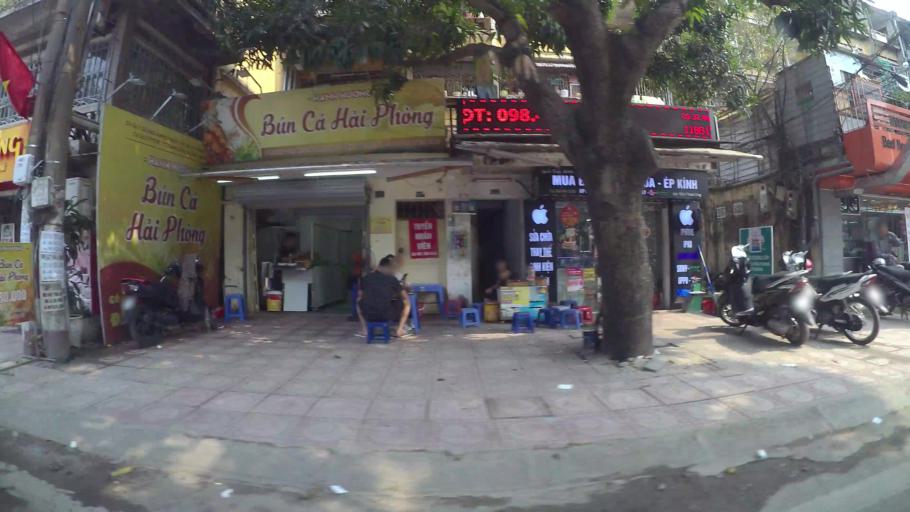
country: VN
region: Ha Noi
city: Dong Da
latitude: 21.0207
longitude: 105.8151
